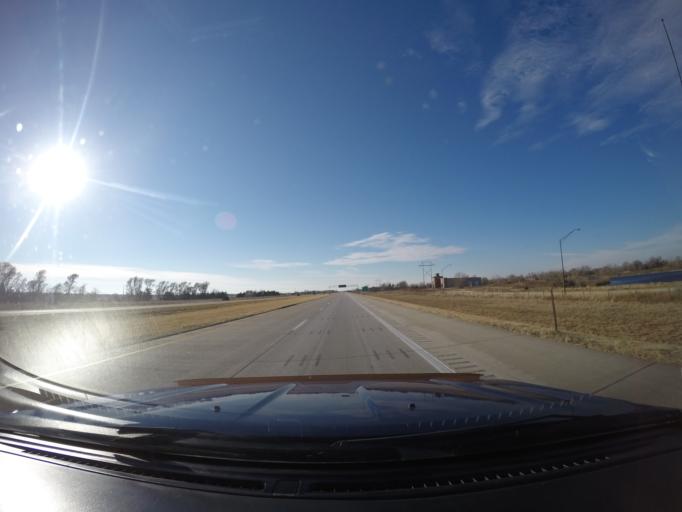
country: US
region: Nebraska
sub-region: Buffalo County
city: Kearney
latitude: 40.6699
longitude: -99.0429
